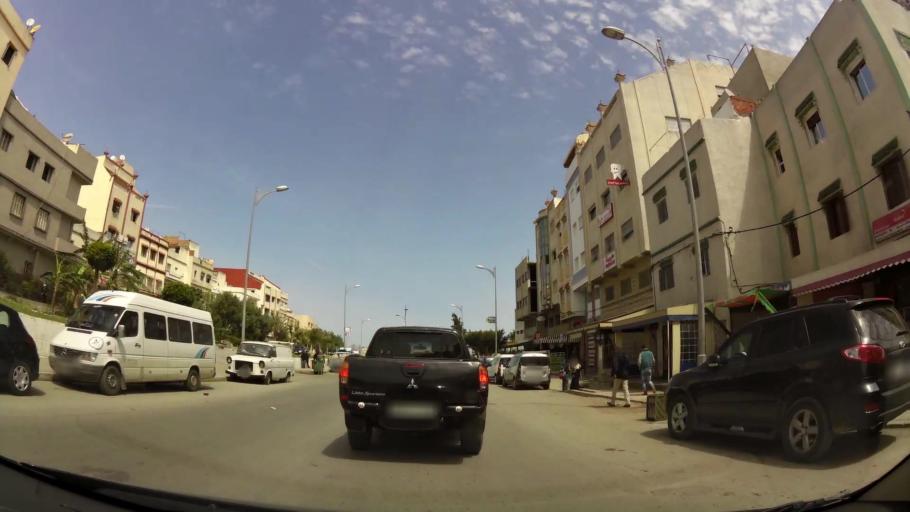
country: MA
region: Tanger-Tetouan
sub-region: Tanger-Assilah
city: Tangier
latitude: 35.7471
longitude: -5.8293
